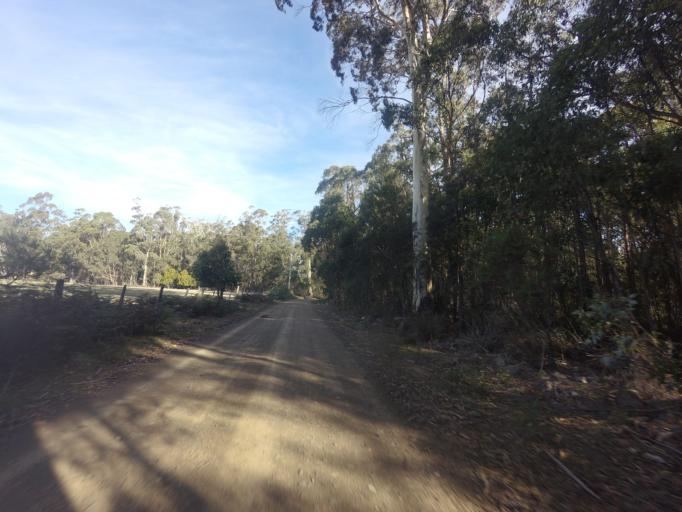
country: AU
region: Tasmania
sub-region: Sorell
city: Sorell
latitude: -42.5118
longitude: 147.4760
